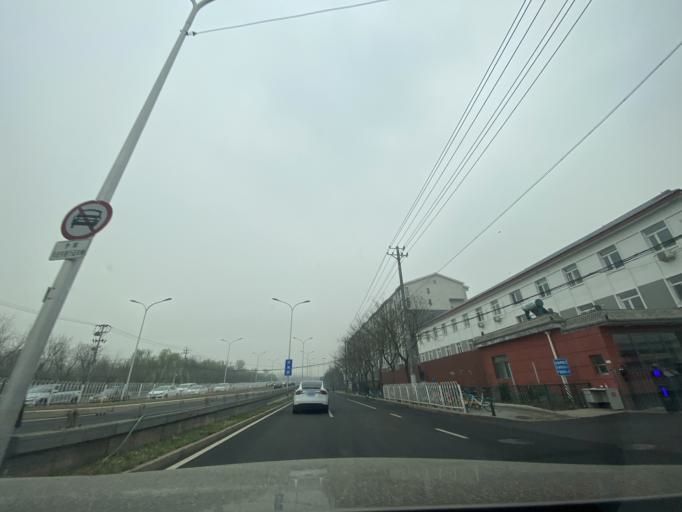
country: CN
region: Beijing
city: Sijiqing
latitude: 39.9685
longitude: 116.2642
